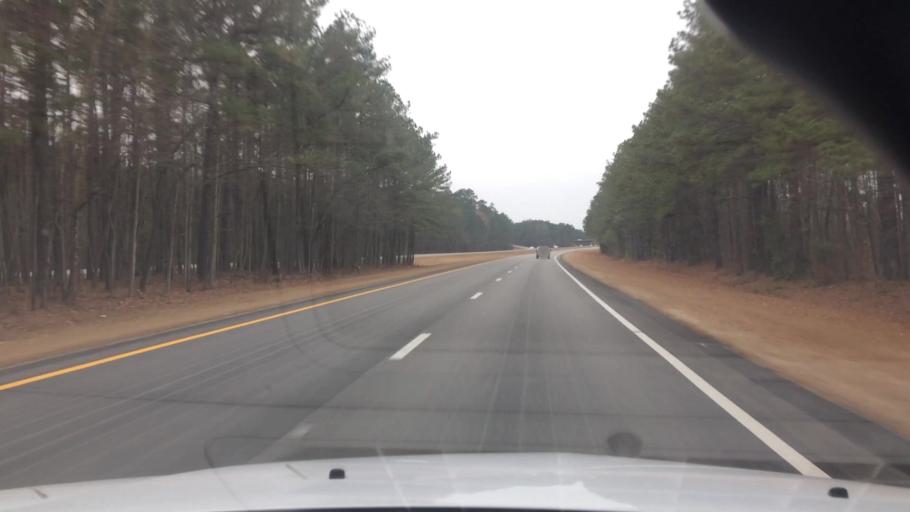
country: US
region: North Carolina
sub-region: Nash County
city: Spring Hope
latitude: 35.9311
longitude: -78.0863
